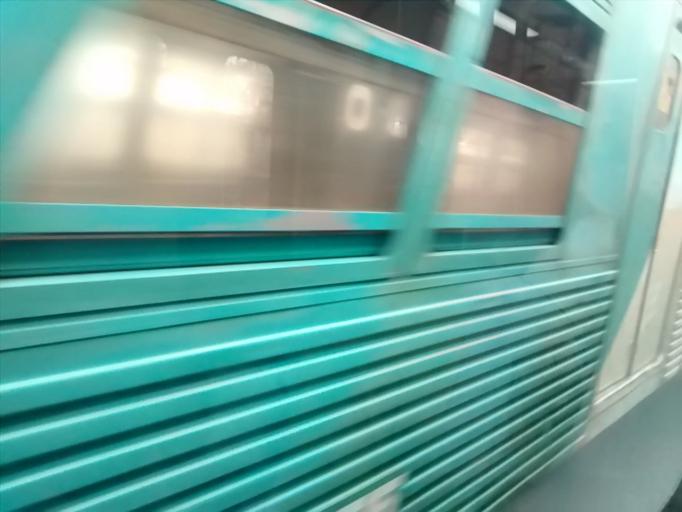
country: BR
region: Rio de Janeiro
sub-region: Rio De Janeiro
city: Rio de Janeiro
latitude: -22.9058
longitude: -43.2017
